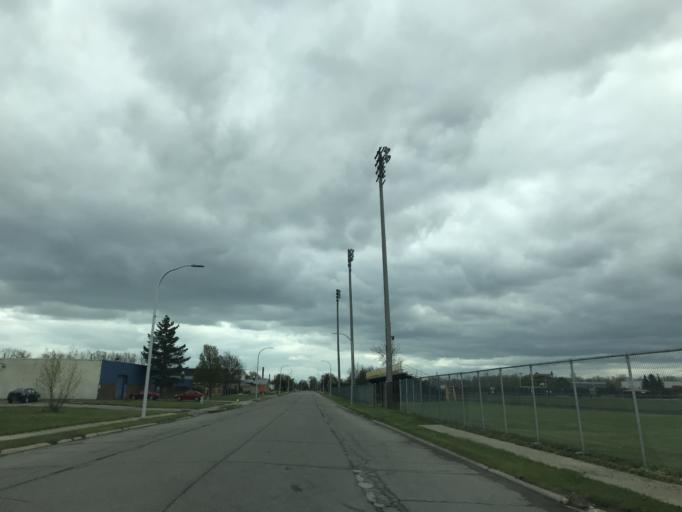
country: US
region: Michigan
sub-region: Wayne County
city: Riverview
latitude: 42.1765
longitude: -83.1743
